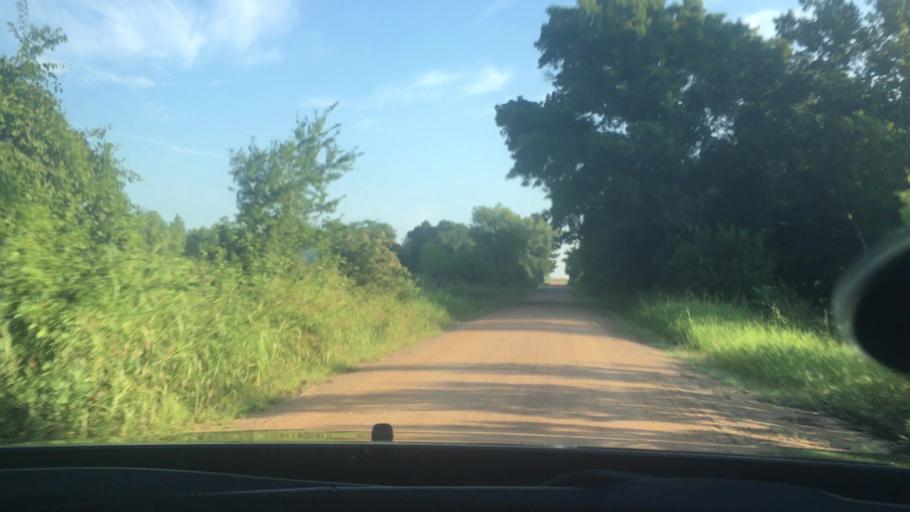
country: US
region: Oklahoma
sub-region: Pontotoc County
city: Ada
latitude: 34.8123
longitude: -96.7749
